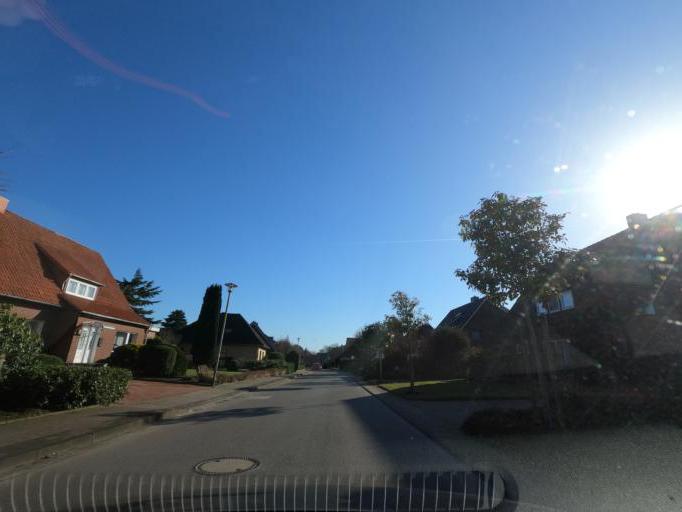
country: DE
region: Lower Saxony
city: Emstek
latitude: 52.8590
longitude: 8.1248
